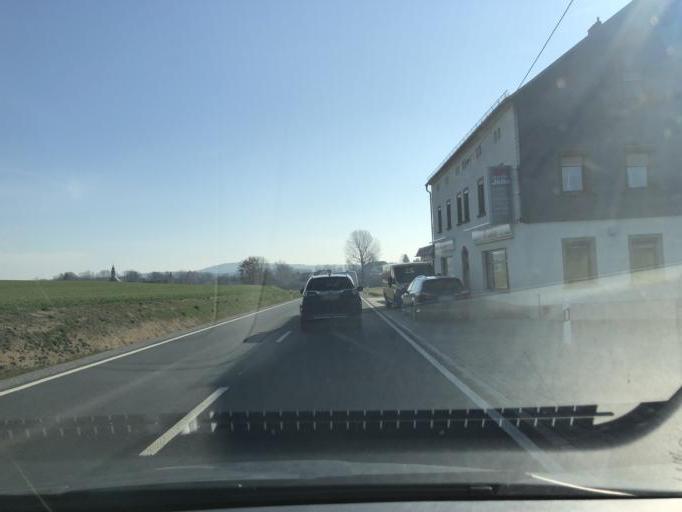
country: DE
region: Saxony
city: Rammenau
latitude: 51.1532
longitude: 14.1258
